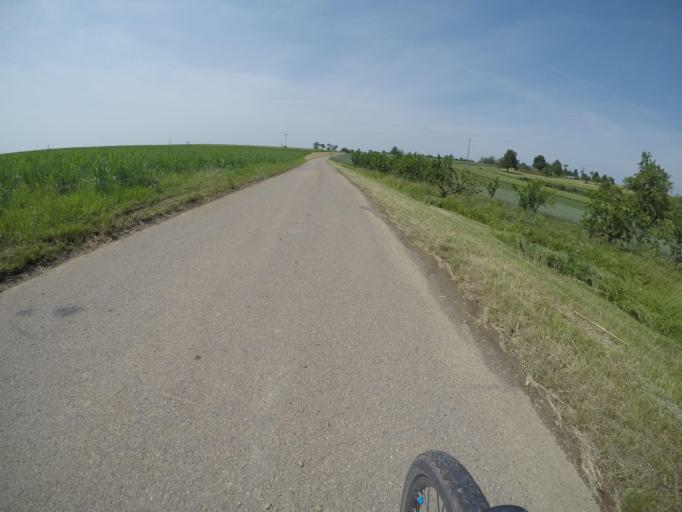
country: DE
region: Baden-Wuerttemberg
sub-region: Regierungsbezirk Stuttgart
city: Deckenpfronn
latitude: 48.6268
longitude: 8.8443
